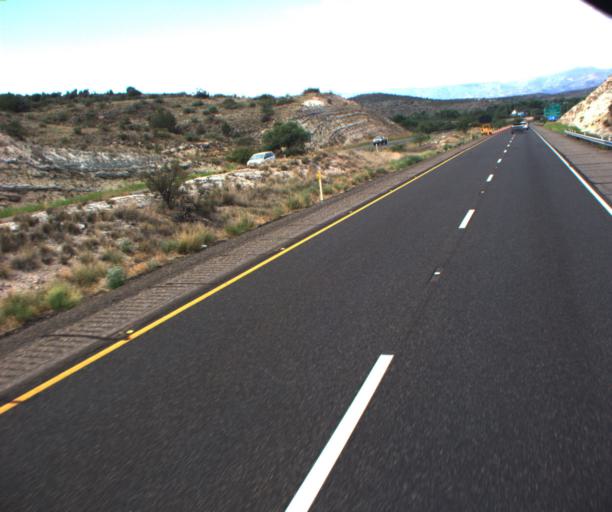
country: US
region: Arizona
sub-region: Yavapai County
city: Lake Montezuma
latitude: 34.6441
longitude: -111.8072
